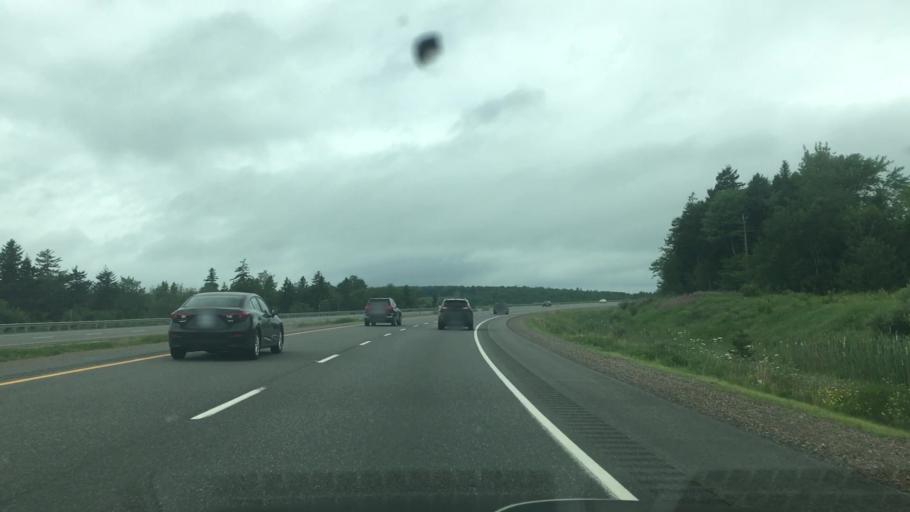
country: CA
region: Nova Scotia
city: Oxford
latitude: 45.4548
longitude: -63.6363
